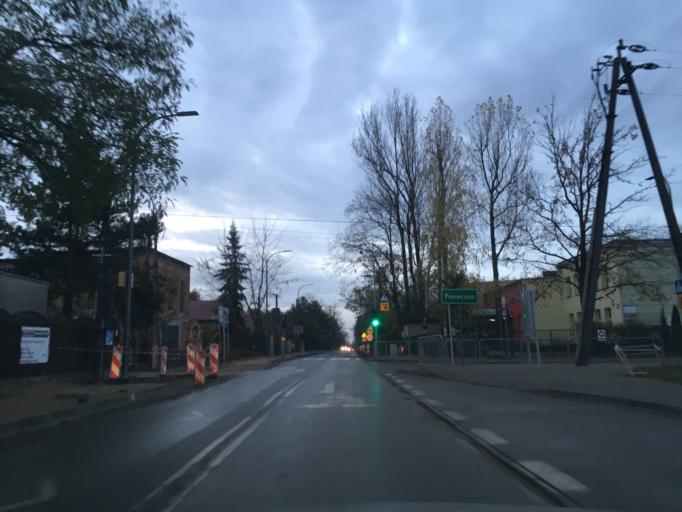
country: PL
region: Masovian Voivodeship
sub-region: Powiat piaseczynski
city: Piaseczno
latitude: 52.0564
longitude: 20.9832
